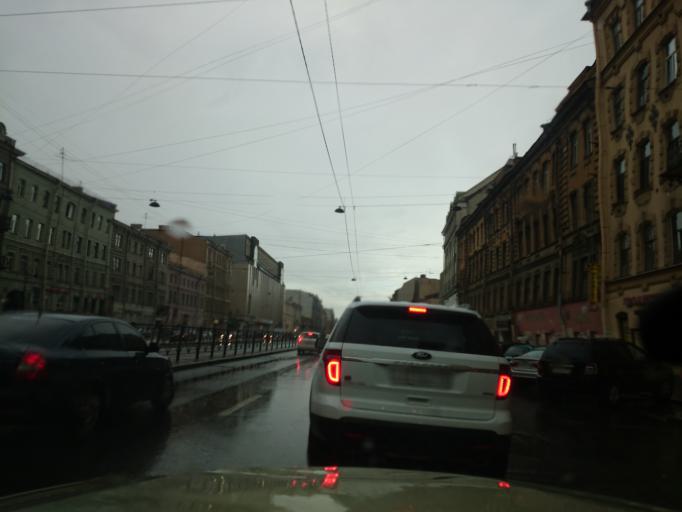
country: RU
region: St.-Petersburg
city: Centralniy
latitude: 59.9240
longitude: 30.3568
